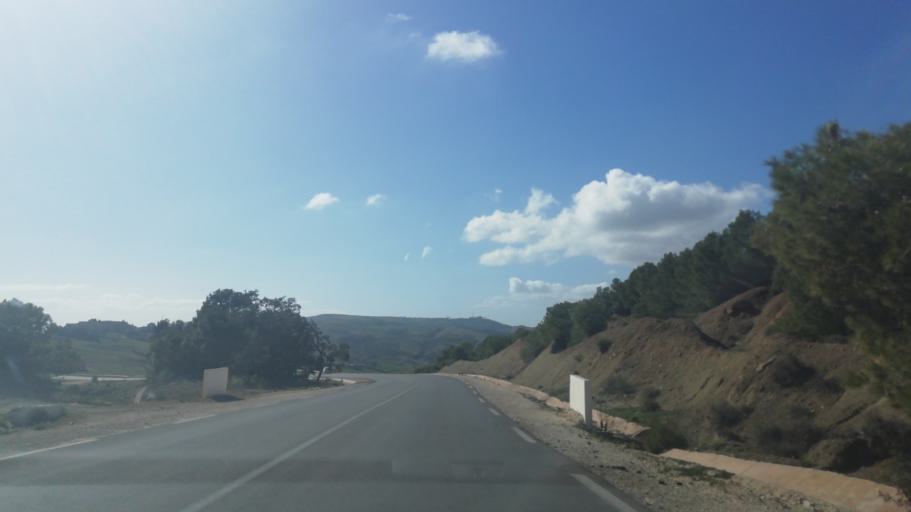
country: DZ
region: Relizane
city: Djidiouia
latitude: 36.0913
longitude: 0.5179
